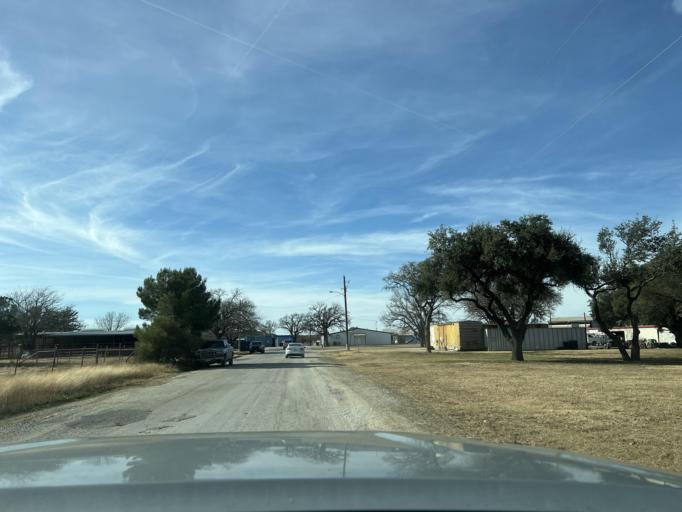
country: US
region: Texas
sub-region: Eastland County
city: Eastland
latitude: 32.4001
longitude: -98.7964
